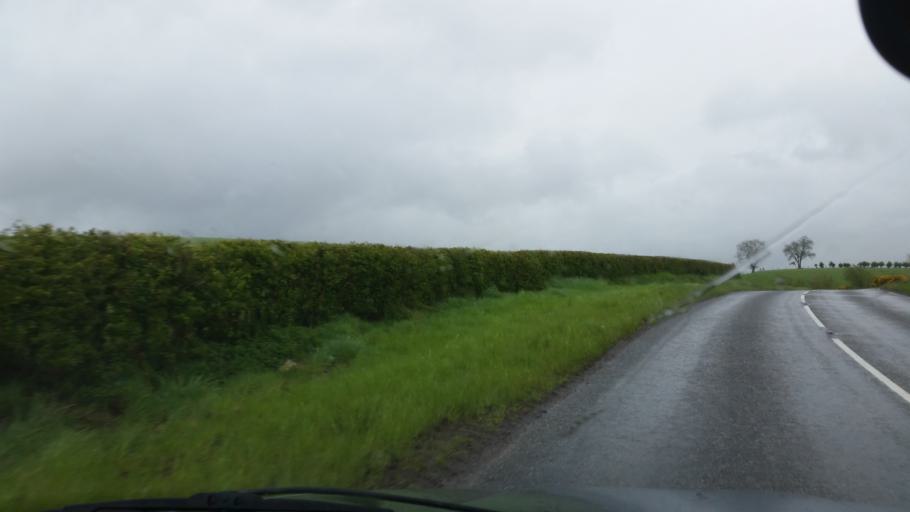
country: GB
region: Northern Ireland
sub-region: Omagh District
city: Omagh
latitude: 54.5698
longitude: -7.2768
